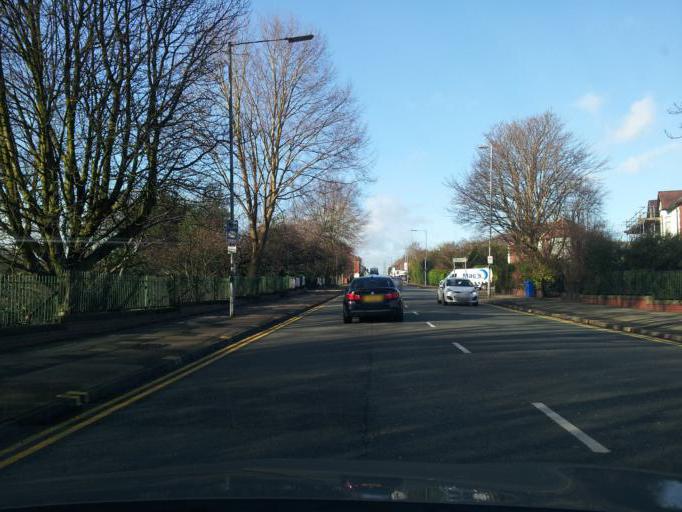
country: GB
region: England
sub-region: Borough of Bury
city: Prestwich
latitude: 53.5284
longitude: -2.2810
